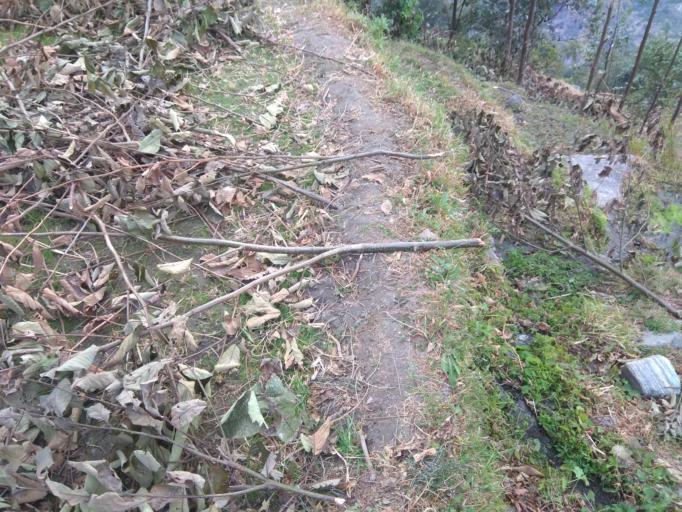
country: NP
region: Far Western
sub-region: Seti Zone
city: Achham
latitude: 29.2325
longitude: 81.6424
